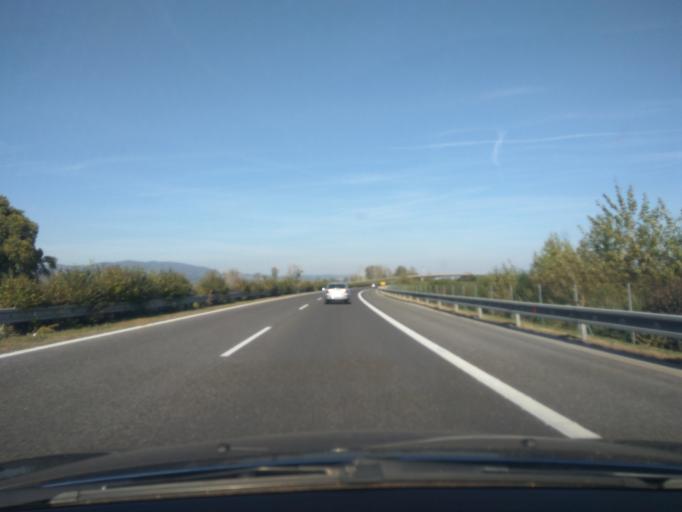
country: SK
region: Trenciansky
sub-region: Okres Nove Mesto nad Vahom
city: Nove Mesto nad Vahom
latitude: 48.8188
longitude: 17.9083
